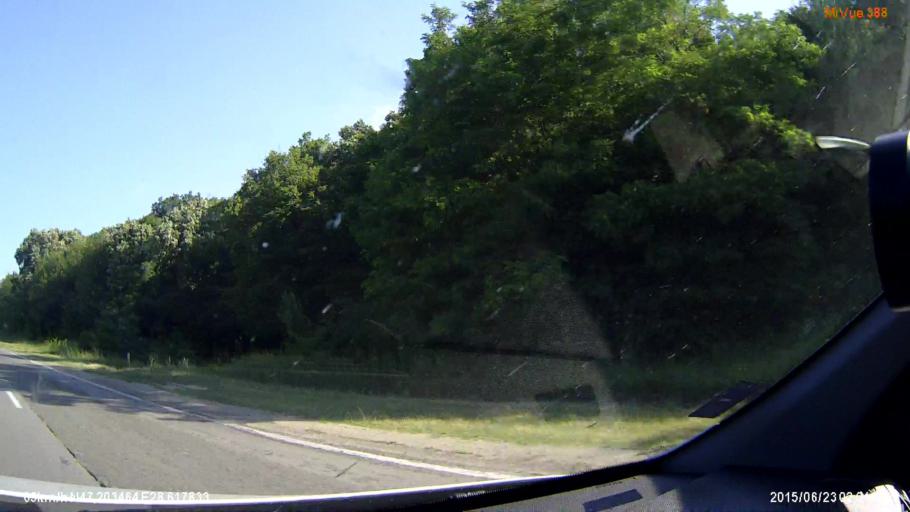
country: MD
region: Straseni
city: Straseni
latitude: 47.2038
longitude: 28.6175
